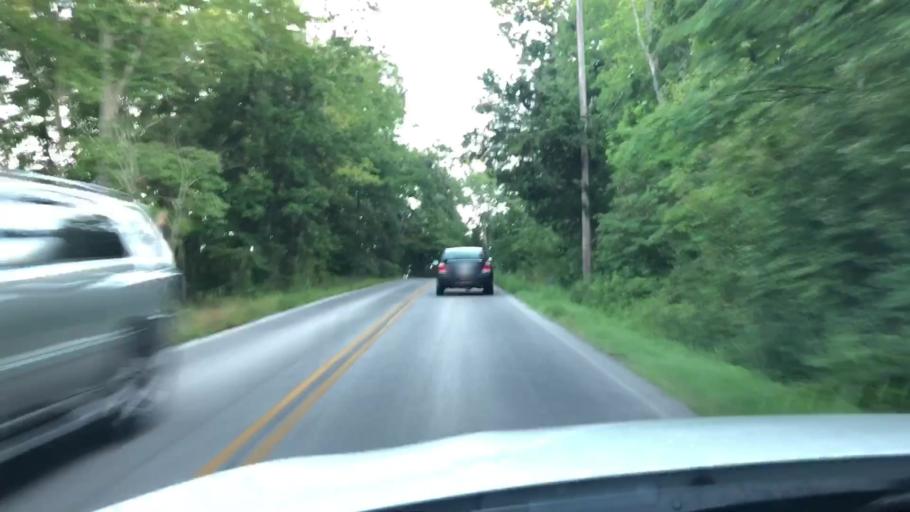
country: US
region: Kentucky
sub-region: Jefferson County
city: Middletown
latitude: 38.1953
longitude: -85.4907
